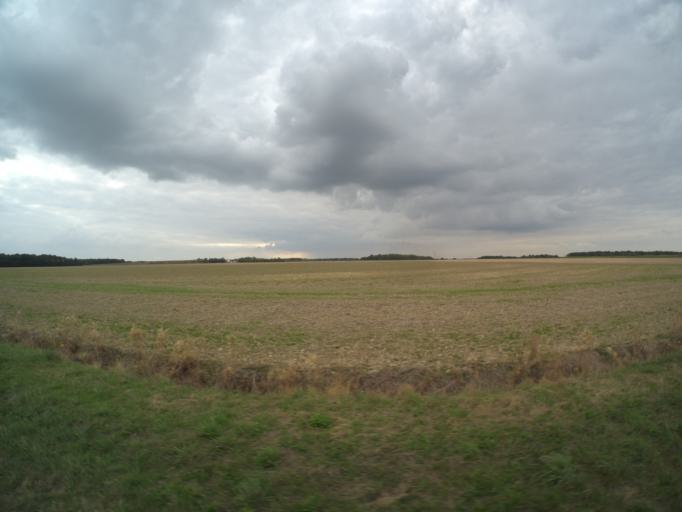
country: FR
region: Centre
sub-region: Departement d'Indre-et-Loire
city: Auzouer-en-Touraine
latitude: 47.4949
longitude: 0.9472
